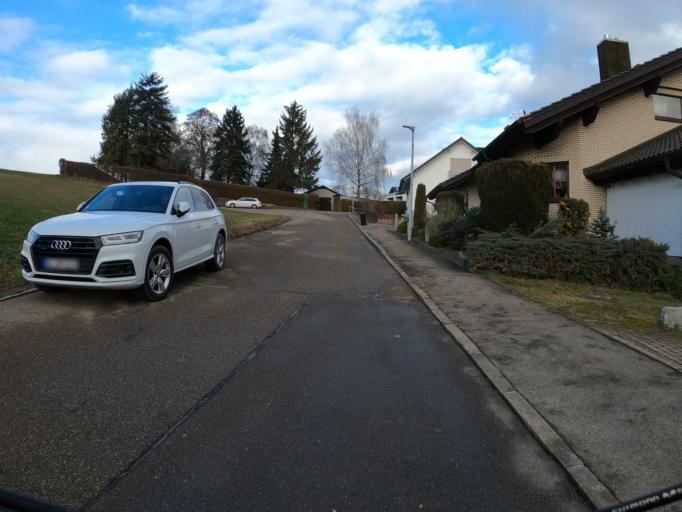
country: DE
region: Bavaria
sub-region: Swabia
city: Nersingen
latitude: 48.4586
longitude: 10.0994
